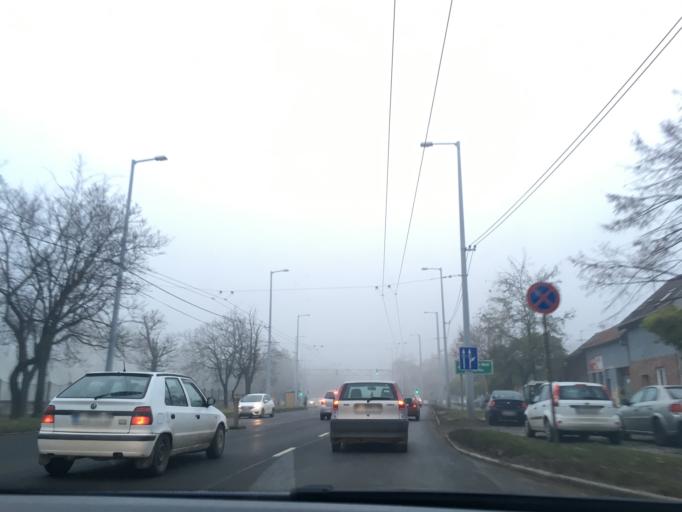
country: HU
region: Hajdu-Bihar
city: Debrecen
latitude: 47.5289
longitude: 21.6387
